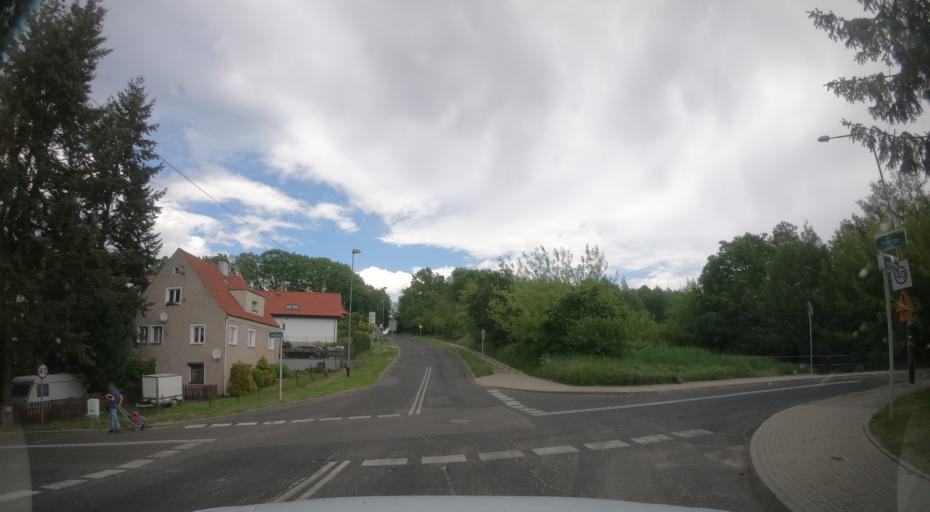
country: PL
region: West Pomeranian Voivodeship
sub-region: Szczecin
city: Szczecin
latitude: 53.3603
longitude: 14.6027
